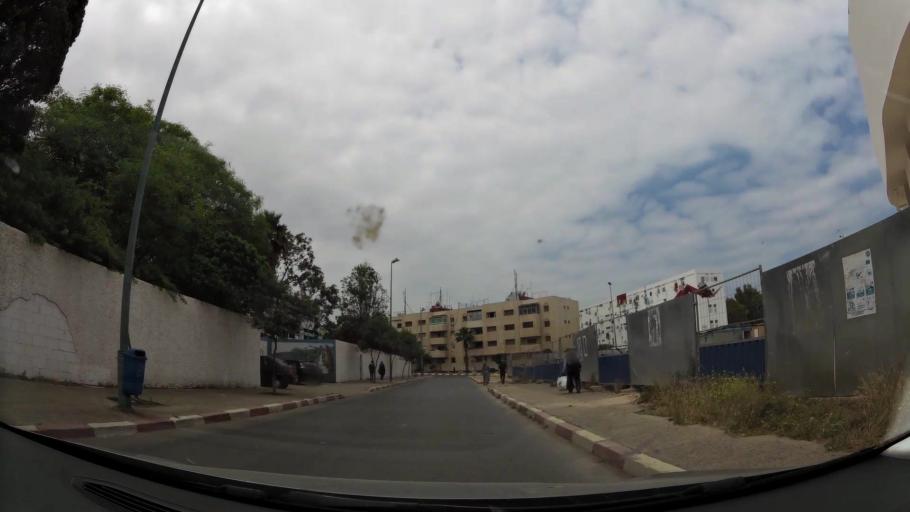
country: MA
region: Rabat-Sale-Zemmour-Zaer
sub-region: Rabat
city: Rabat
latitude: 33.9972
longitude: -6.8665
